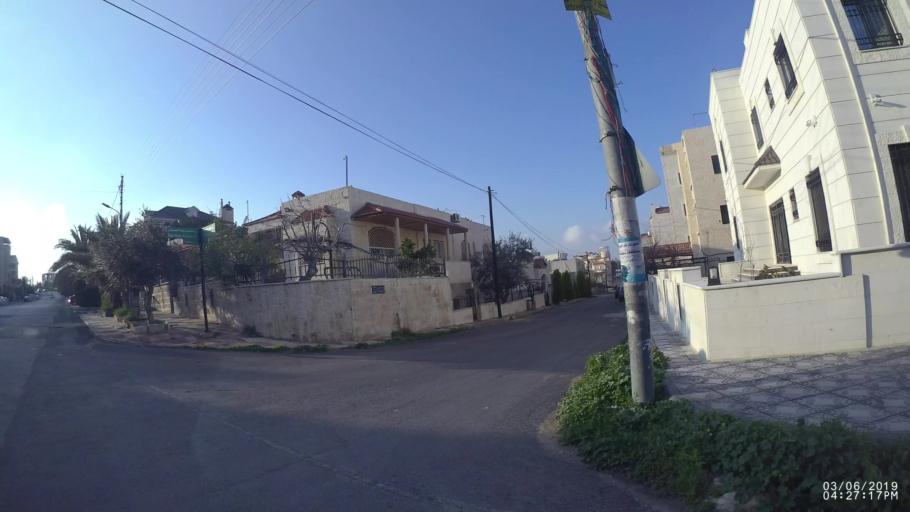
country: JO
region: Amman
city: Amman
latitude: 31.9861
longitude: 35.9601
